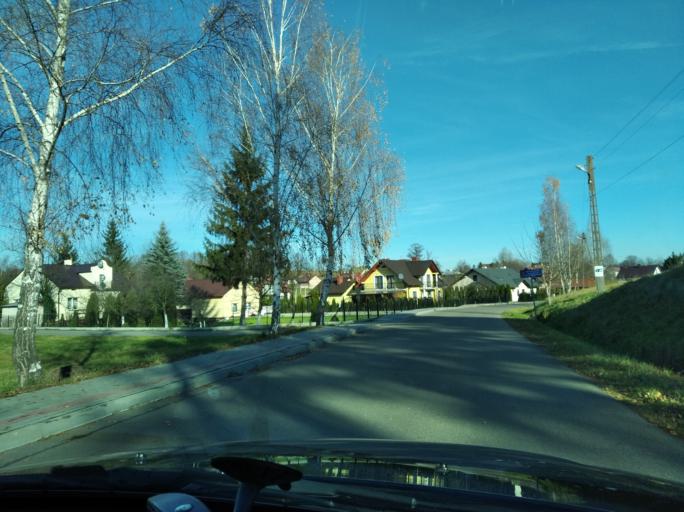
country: PL
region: Subcarpathian Voivodeship
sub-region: Powiat rzeszowski
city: Lutoryz
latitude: 49.9649
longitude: 21.8981
